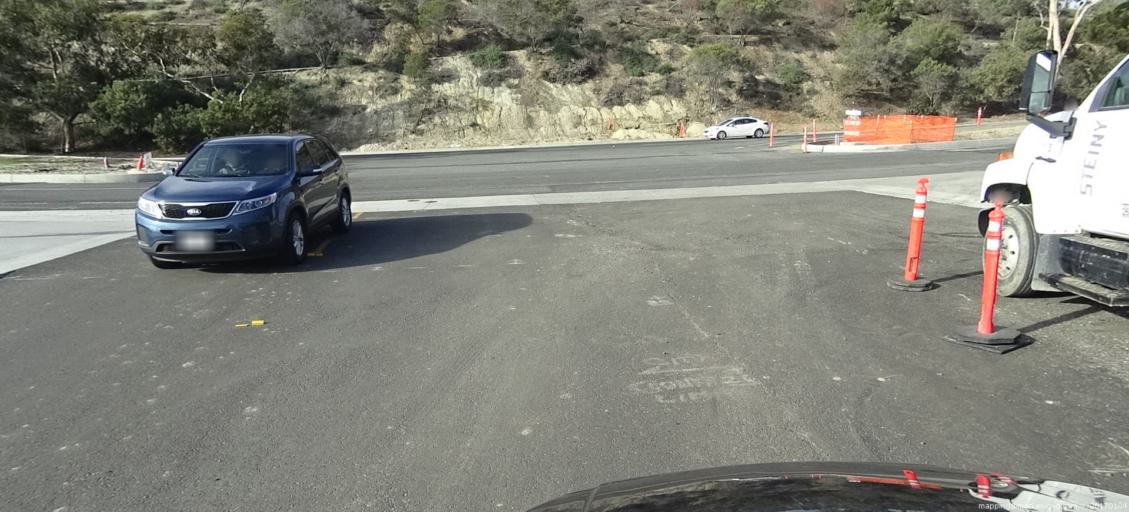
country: US
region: California
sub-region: Orange County
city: Dana Point
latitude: 33.4626
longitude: -117.6899
